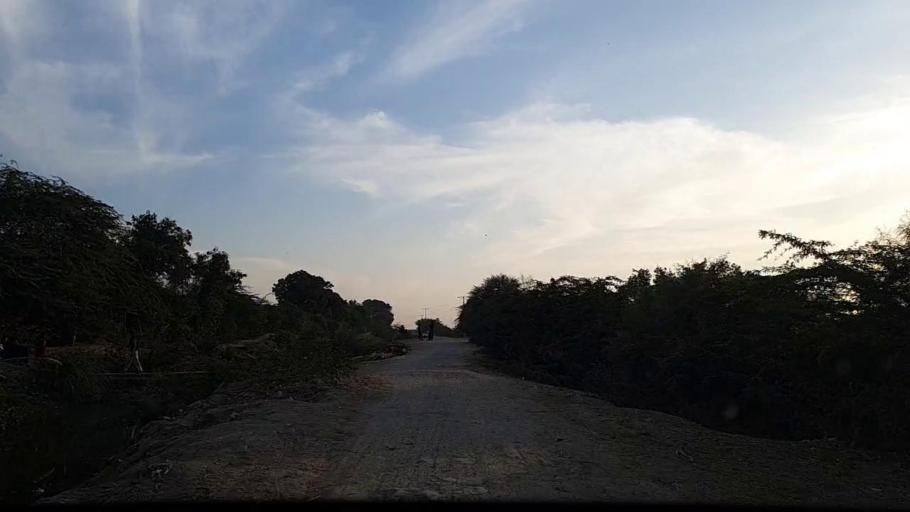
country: PK
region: Sindh
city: Mirpur Batoro
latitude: 24.6375
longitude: 68.1370
